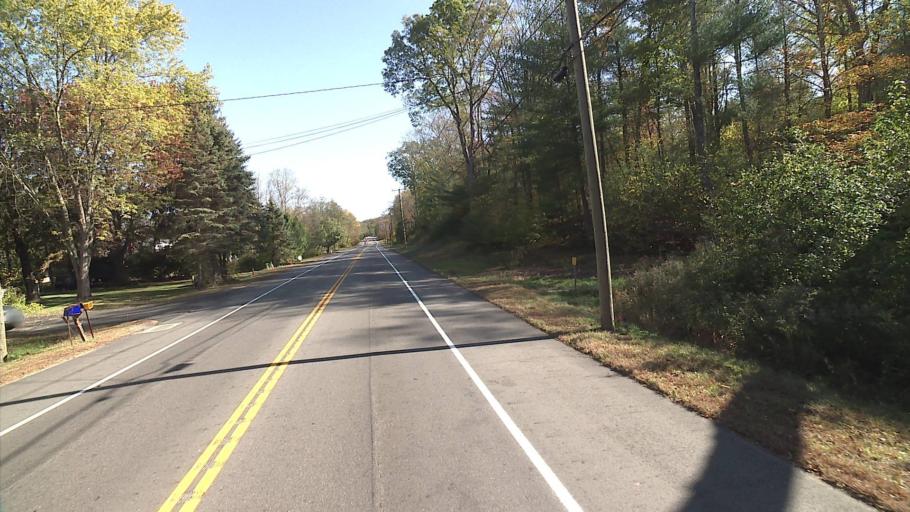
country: US
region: Connecticut
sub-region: Tolland County
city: Coventry Lake
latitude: 41.7294
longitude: -72.3420
